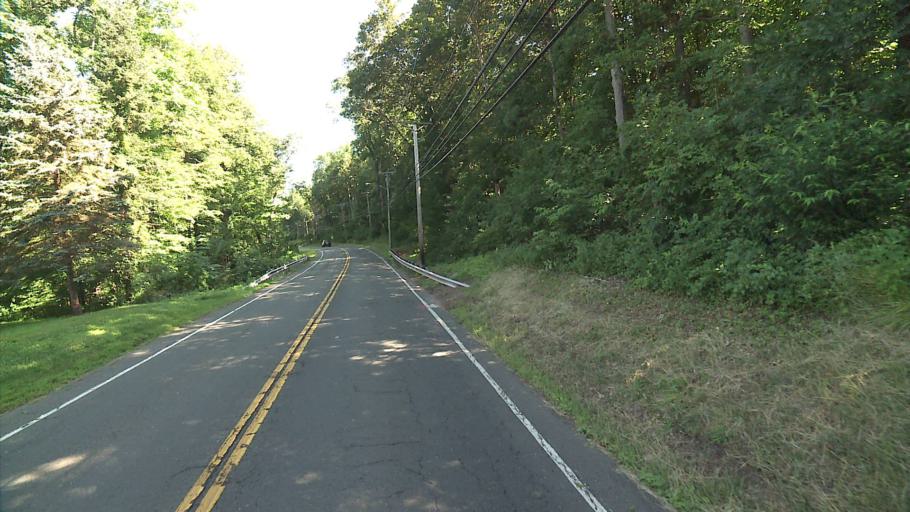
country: US
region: Connecticut
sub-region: Hartford County
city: Farmington
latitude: 41.7348
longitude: -72.8203
